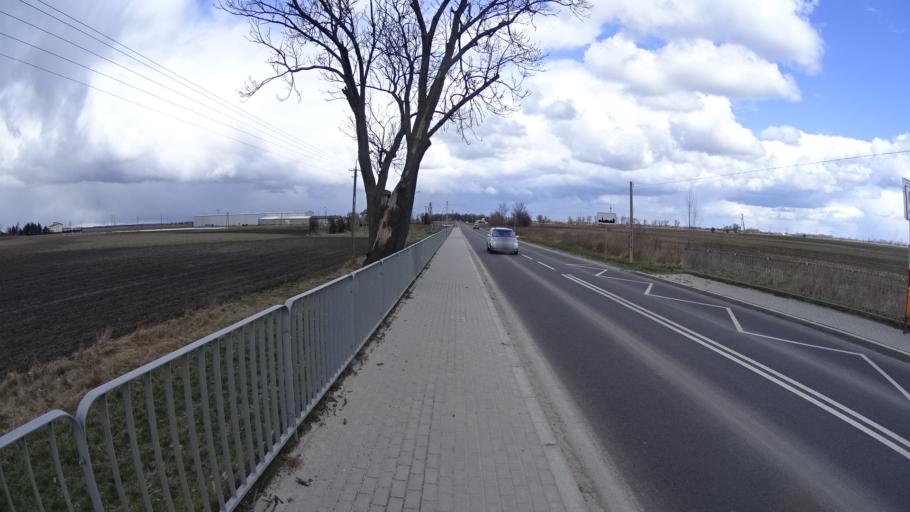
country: PL
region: Masovian Voivodeship
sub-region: Powiat warszawski zachodni
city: Jozefow
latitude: 52.2186
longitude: 20.6922
